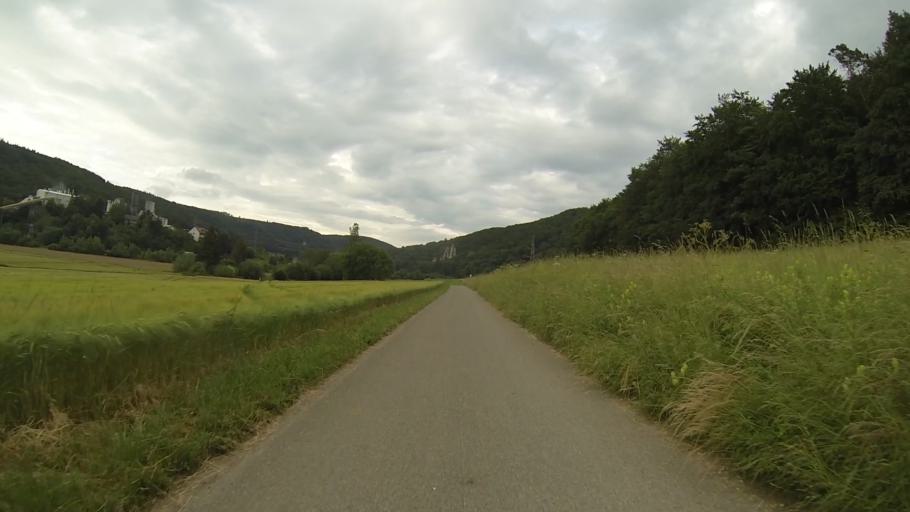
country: DE
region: Baden-Wuerttemberg
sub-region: Tuebingen Region
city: Blaubeuren
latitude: 48.3985
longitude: 9.8262
